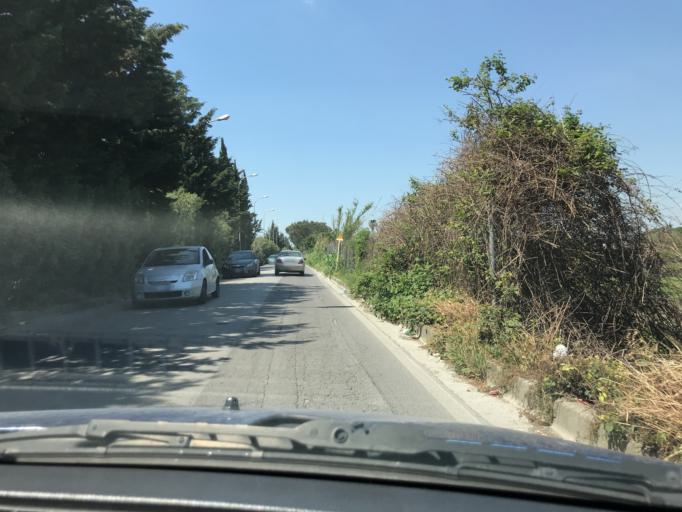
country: IT
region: Campania
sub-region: Provincia di Napoli
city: Calvizzano
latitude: 40.9094
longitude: 14.1949
